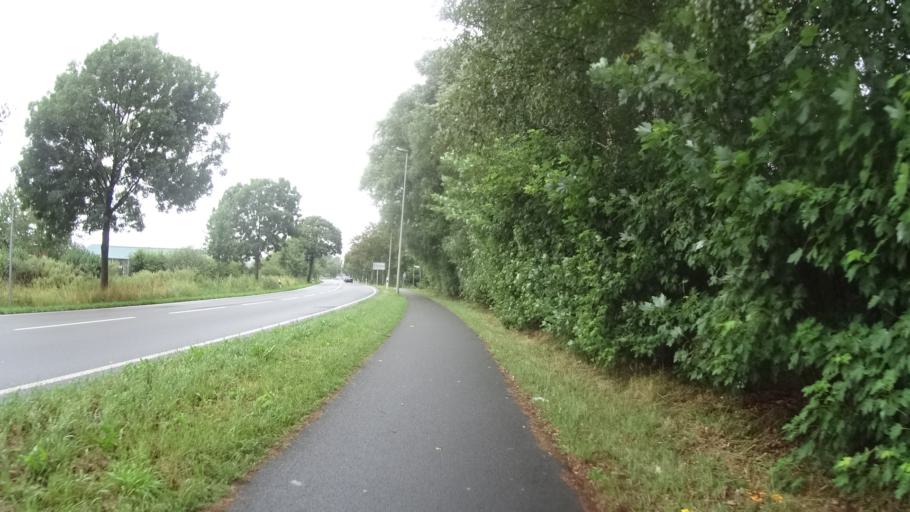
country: DE
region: Lower Saxony
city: Leer
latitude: 53.2189
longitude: 7.4362
